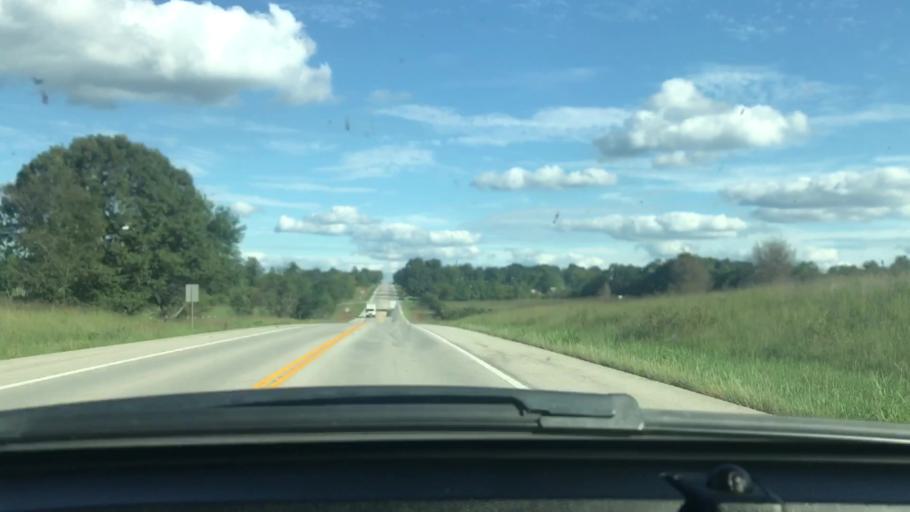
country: US
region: Missouri
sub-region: Howell County
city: West Plains
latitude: 36.6562
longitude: -91.6996
